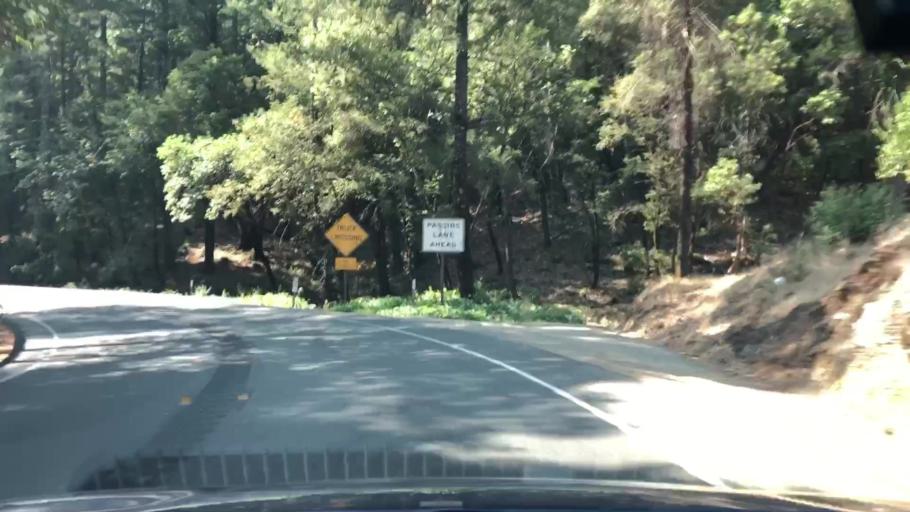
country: US
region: California
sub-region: Lake County
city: Middletown
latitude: 38.6737
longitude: -122.5915
